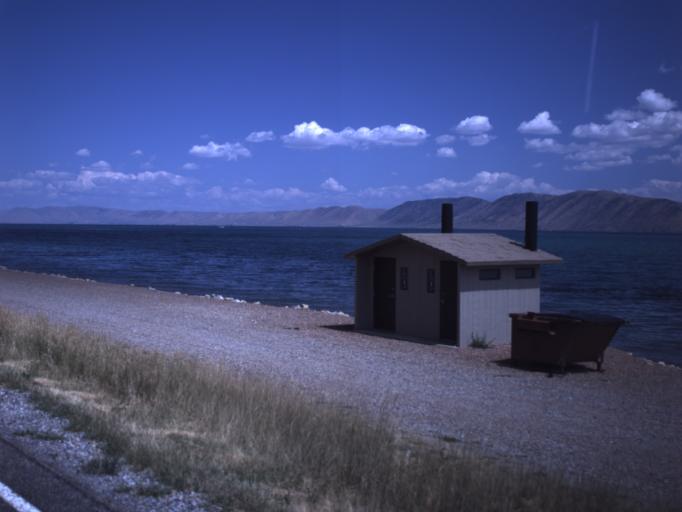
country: US
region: Utah
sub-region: Rich County
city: Randolph
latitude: 41.8920
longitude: -111.3664
